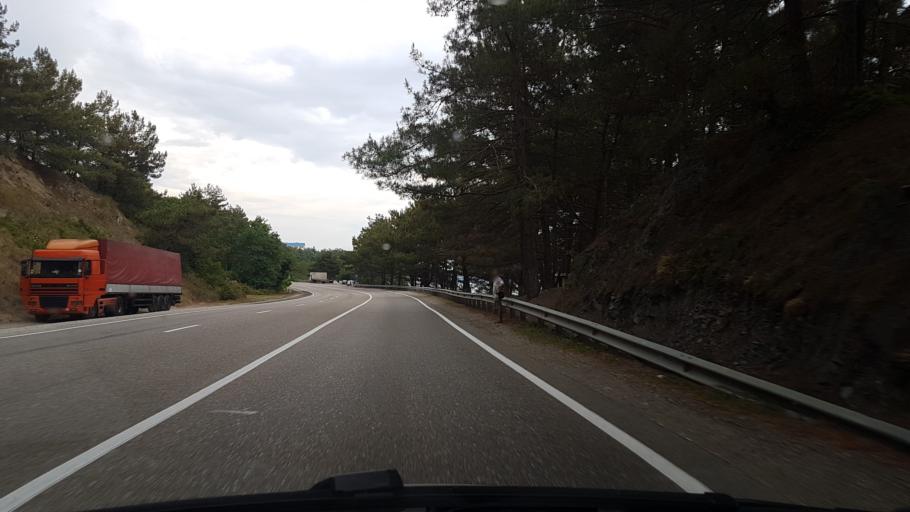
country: RU
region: Krasnodarskiy
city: Ol'ginka
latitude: 44.1855
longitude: 38.9191
